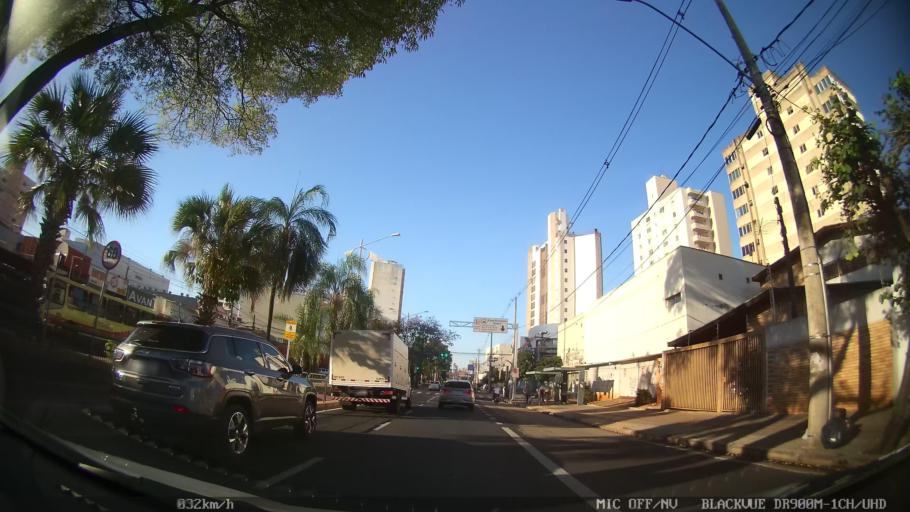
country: BR
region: Sao Paulo
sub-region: Sao Jose Do Rio Preto
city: Sao Jose do Rio Preto
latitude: -20.8093
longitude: -49.3830
